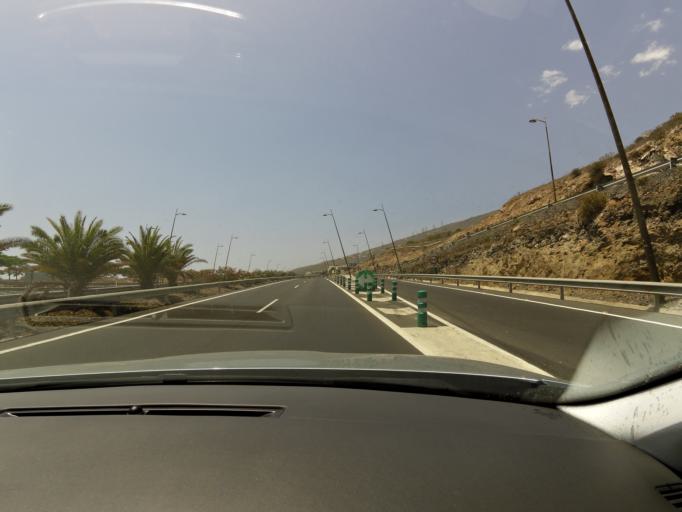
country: ES
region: Canary Islands
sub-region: Provincia de Santa Cruz de Tenerife
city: Adeje
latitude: 28.1149
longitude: -16.7358
